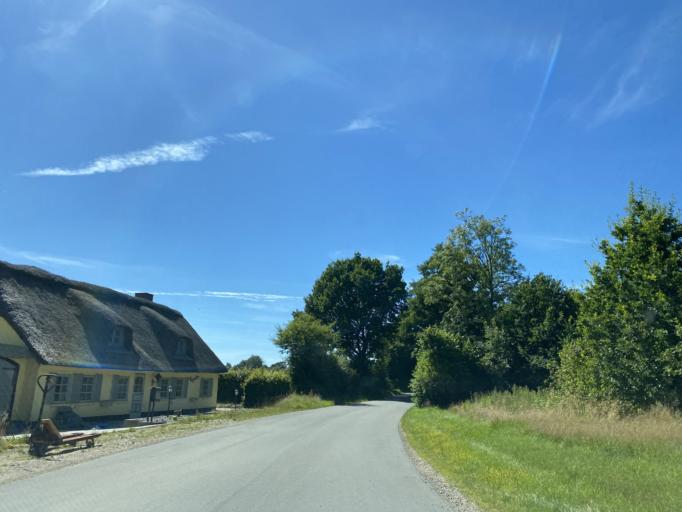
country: DK
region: South Denmark
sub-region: Kolding Kommune
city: Christiansfeld
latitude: 55.3760
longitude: 9.4855
